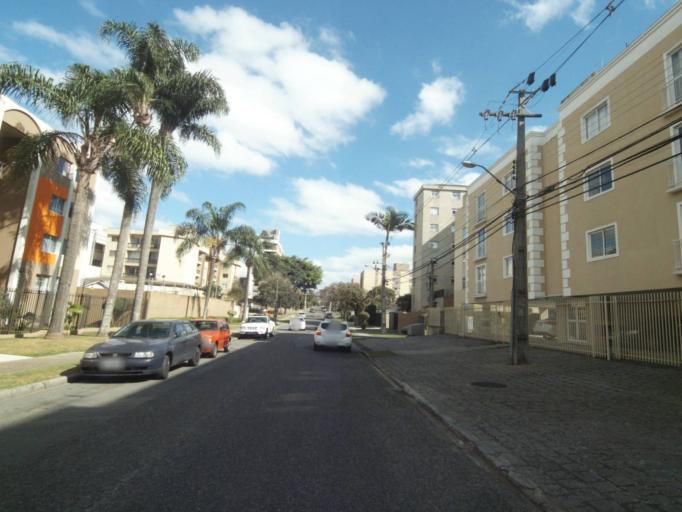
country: BR
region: Parana
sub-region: Curitiba
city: Curitiba
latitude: -25.4639
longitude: -49.2854
